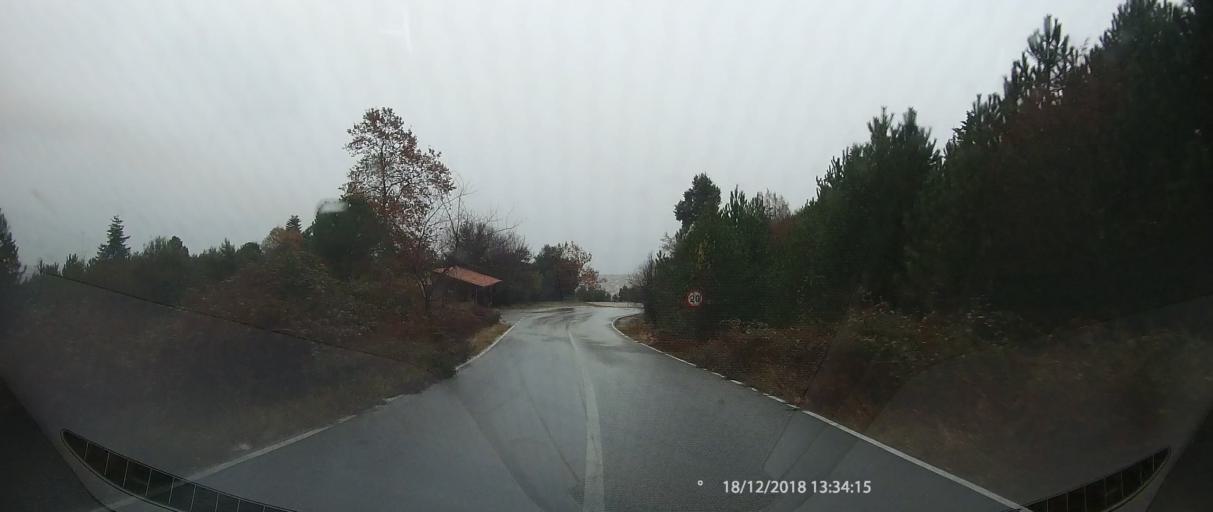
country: GR
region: Central Macedonia
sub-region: Nomos Pierias
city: Litochoro
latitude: 40.1133
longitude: 22.4850
